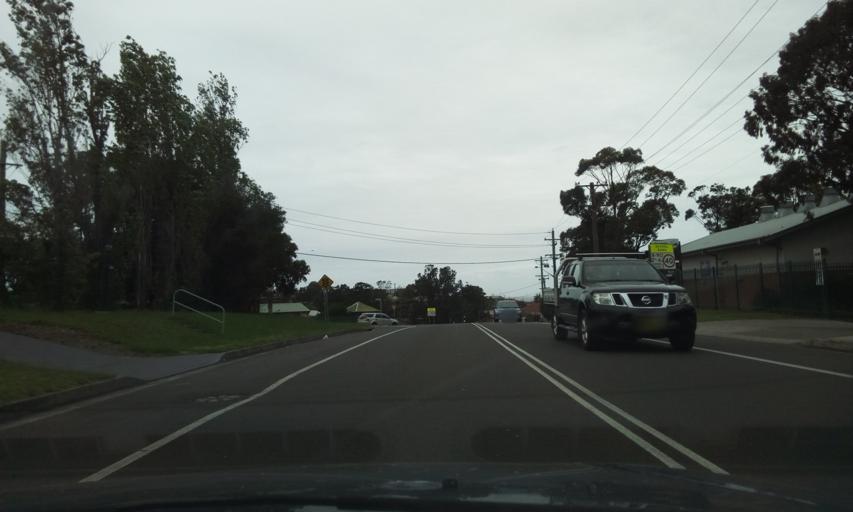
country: AU
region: New South Wales
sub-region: Wollongong
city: Lake Heights
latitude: -34.4802
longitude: 150.8779
